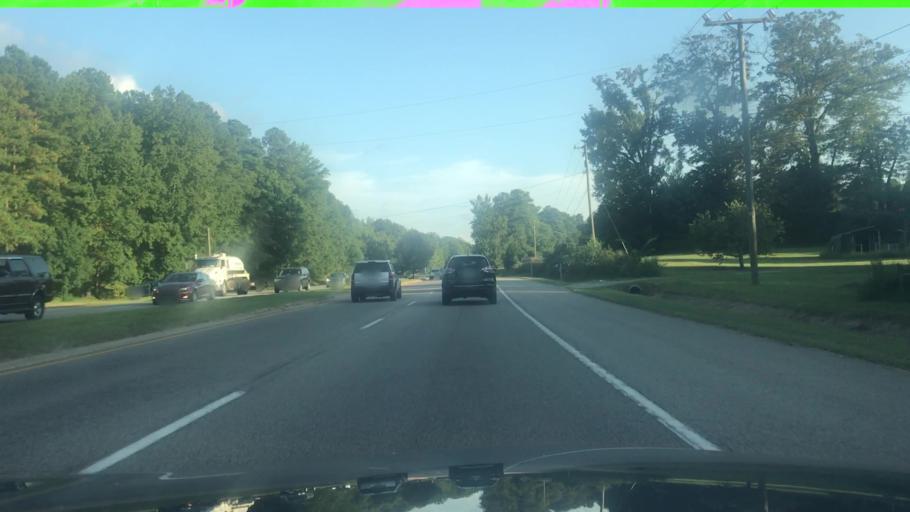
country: US
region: Virginia
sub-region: Chesterfield County
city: Brandermill
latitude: 37.4520
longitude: -77.5864
